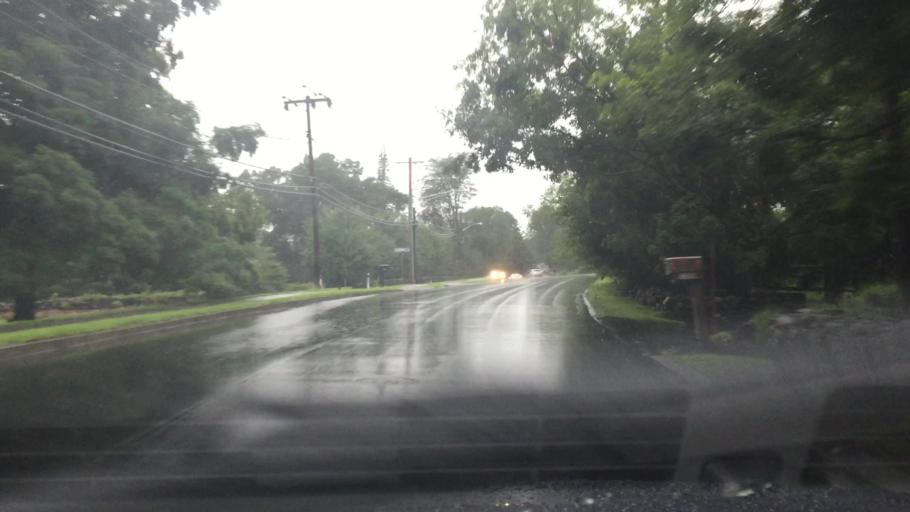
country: US
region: Massachusetts
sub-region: Middlesex County
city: Tewksbury
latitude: 42.6420
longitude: -71.2526
